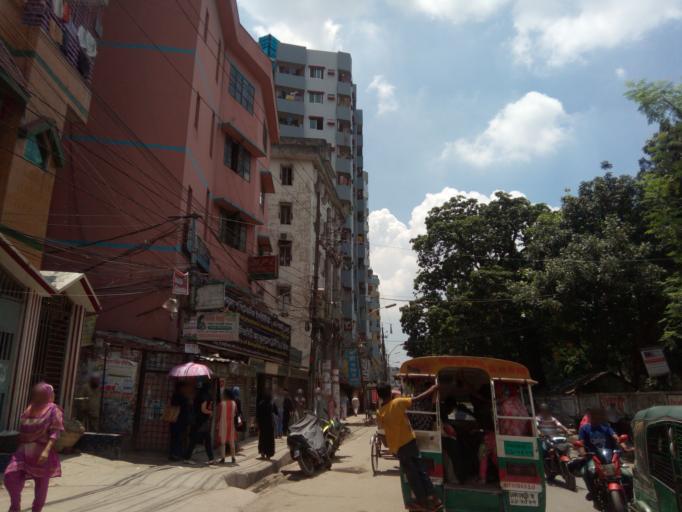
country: BD
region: Dhaka
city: Azimpur
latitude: 23.7572
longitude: 90.3931
